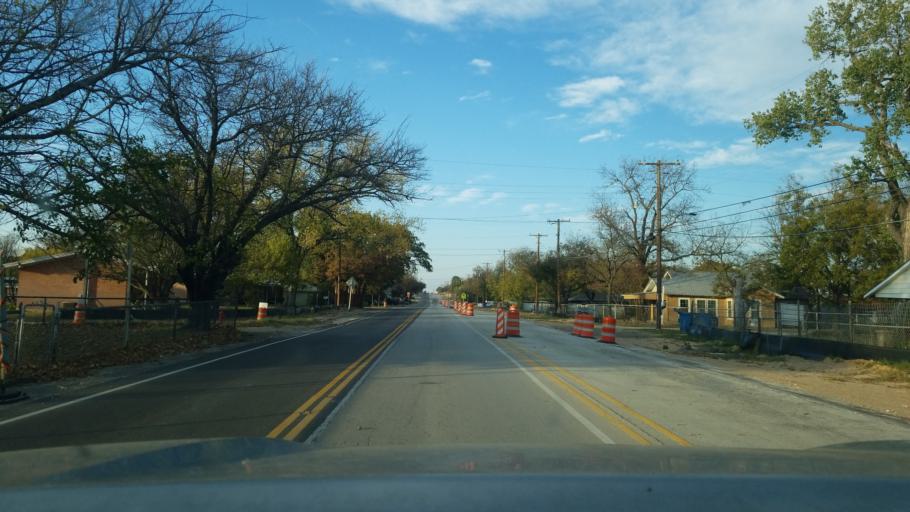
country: US
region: Texas
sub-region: Brown County
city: Lake Brownwood
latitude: 32.1014
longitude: -98.9643
